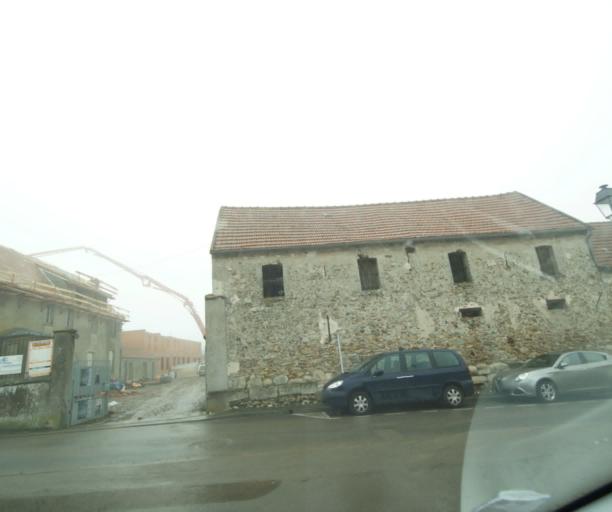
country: FR
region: Ile-de-France
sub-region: Departement de Seine-et-Marne
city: Longperrier
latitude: 49.0509
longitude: 2.6636
